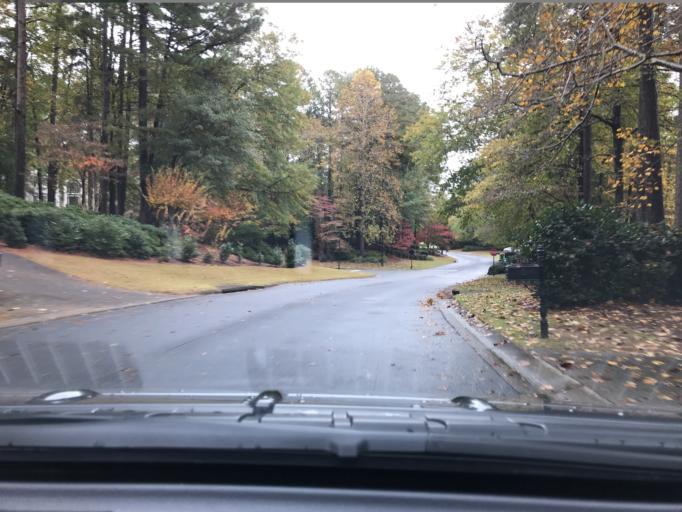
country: US
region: Georgia
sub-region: Fulton County
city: Johns Creek
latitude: 34.0058
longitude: -84.2403
